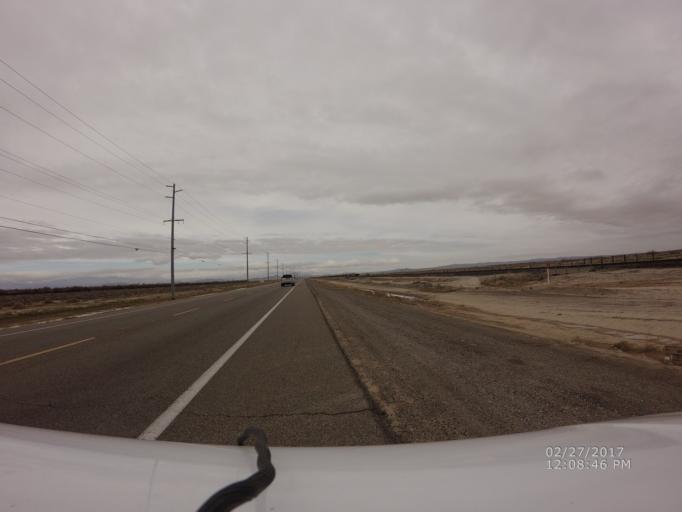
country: US
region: California
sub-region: Los Angeles County
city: Lancaster
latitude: 34.7653
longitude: -118.1471
